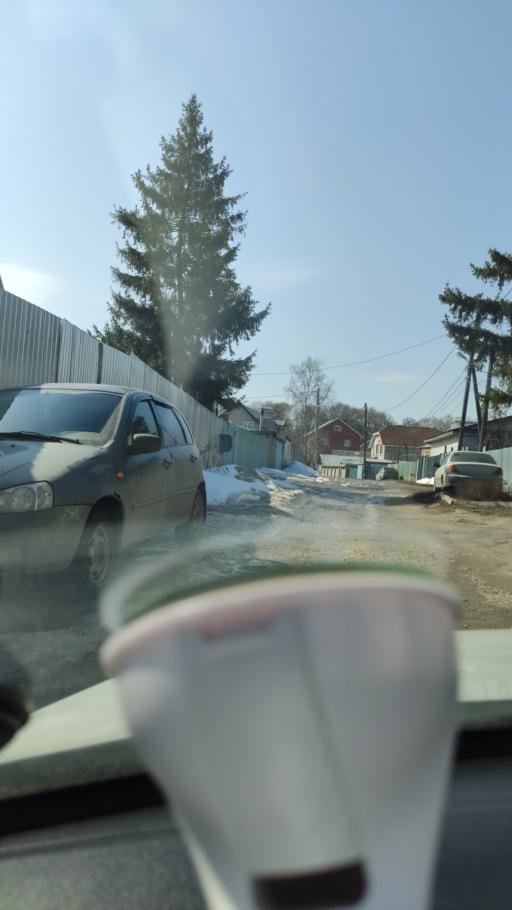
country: RU
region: Samara
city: Petra-Dubrava
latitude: 53.2920
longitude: 50.2797
